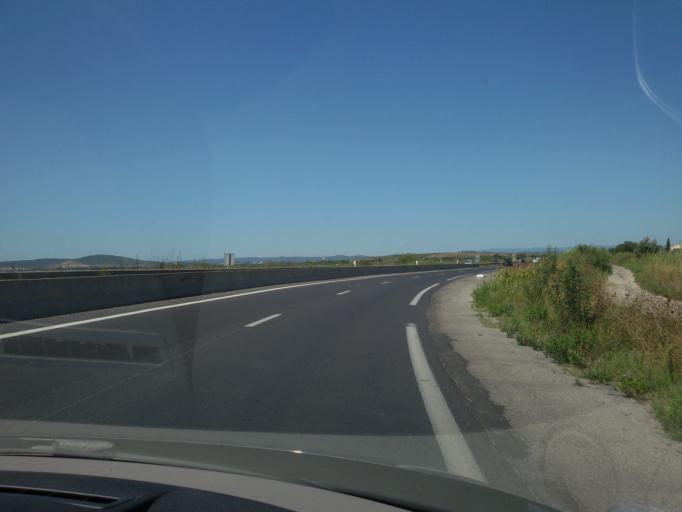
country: FR
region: Languedoc-Roussillon
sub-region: Departement de l'Herault
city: Palavas-les-Flots
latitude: 43.5346
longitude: 3.9064
